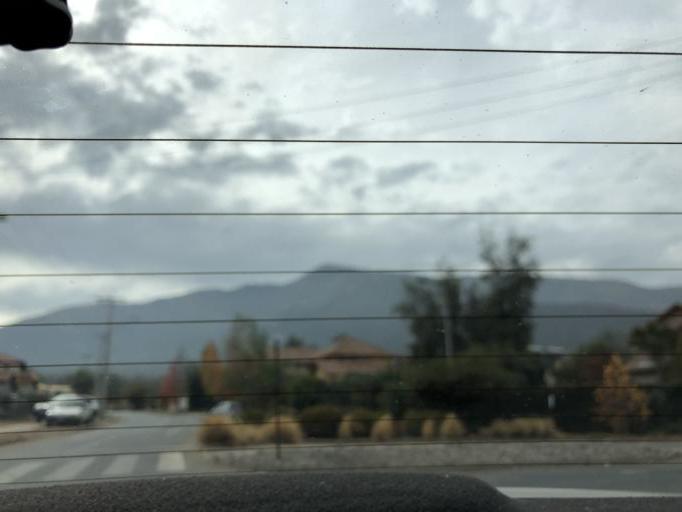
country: CL
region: Santiago Metropolitan
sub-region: Provincia de Cordillera
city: Puente Alto
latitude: -33.5836
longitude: -70.5139
